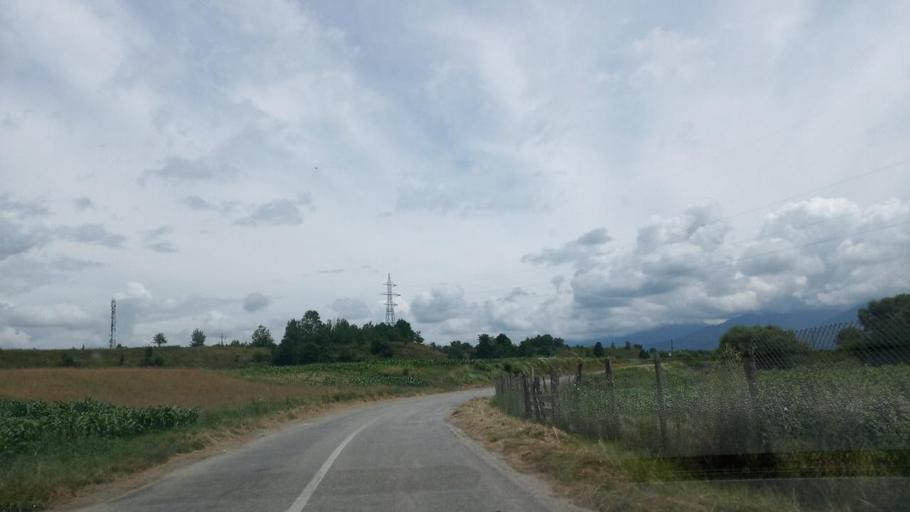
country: RO
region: Sibiu
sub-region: Comuna Porumbacu de Jos
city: Porumbacu de Jos
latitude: 45.7199
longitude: 24.4735
